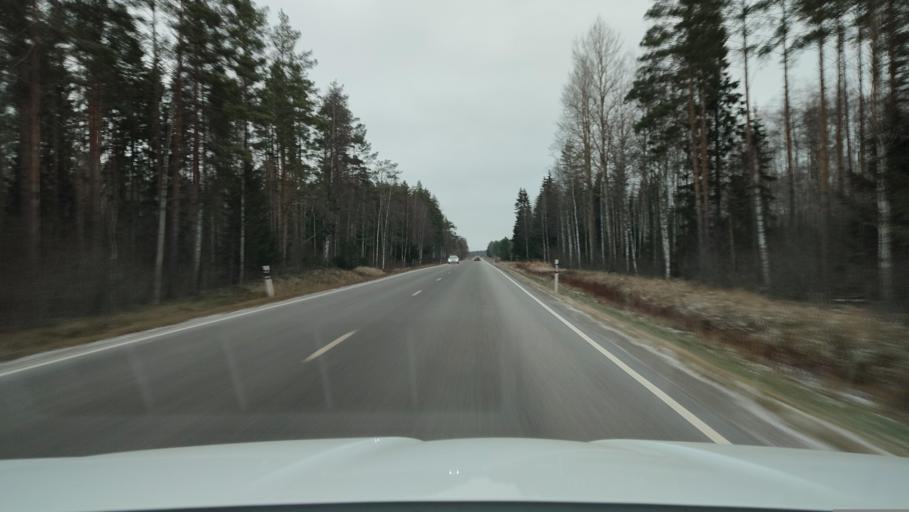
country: FI
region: Ostrobothnia
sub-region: Sydosterbotten
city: Naerpes
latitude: 62.5308
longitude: 21.4624
